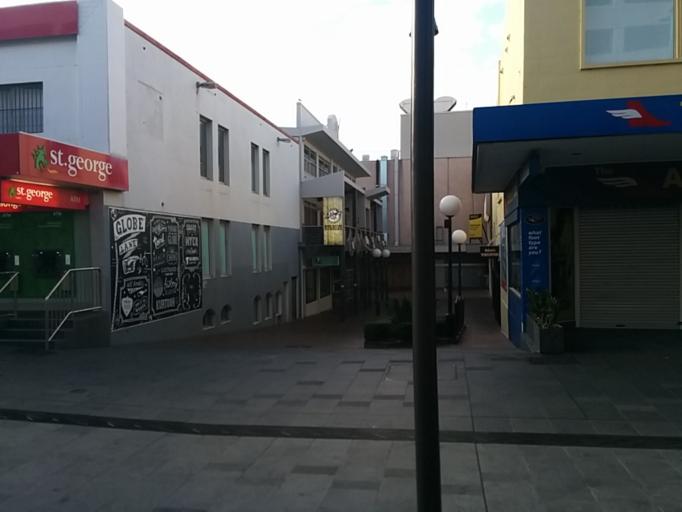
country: AU
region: New South Wales
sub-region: Wollongong
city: Wollongong
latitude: -34.4250
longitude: 150.8938
